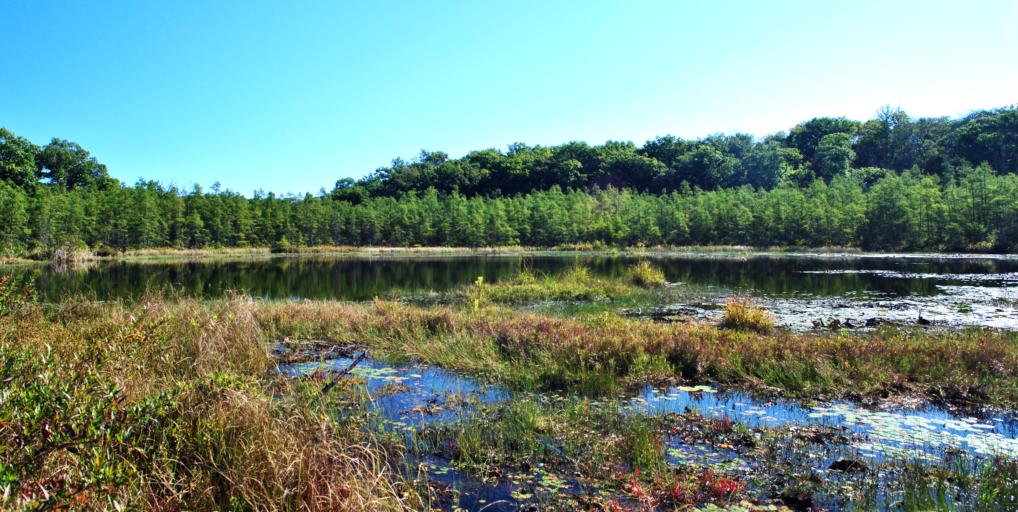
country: US
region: Wisconsin
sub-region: Walworth County
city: East Troy
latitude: 42.8193
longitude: -88.4073
